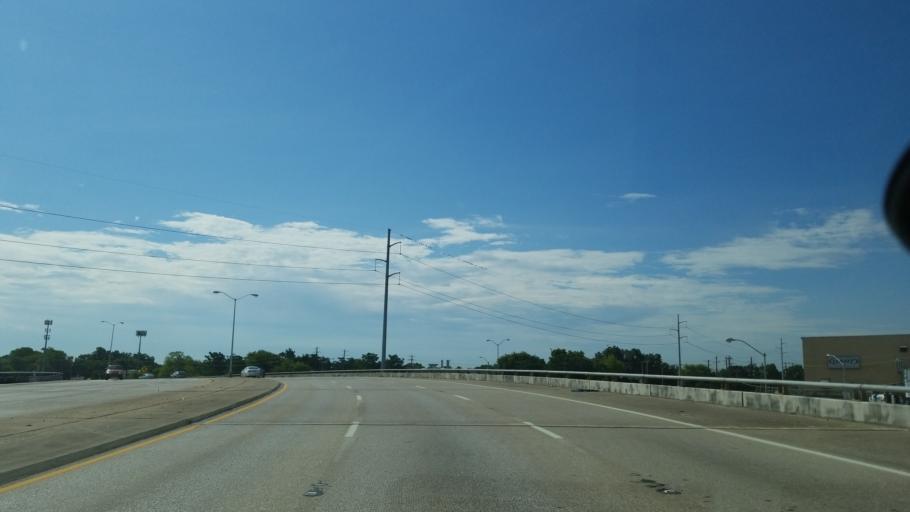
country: US
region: Texas
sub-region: Dallas County
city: Duncanville
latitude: 32.6920
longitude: -96.8921
